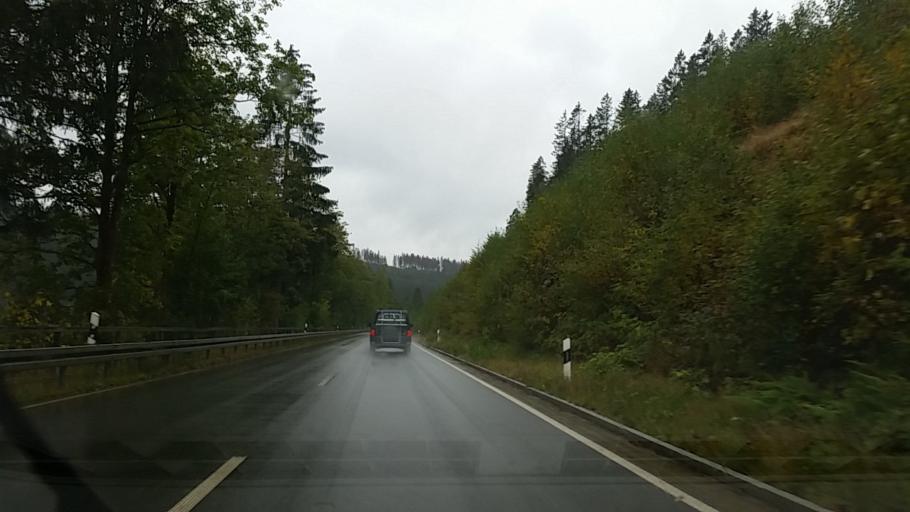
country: DE
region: Lower Saxony
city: Schulenberg im Oberharz
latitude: 51.8344
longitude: 10.4571
